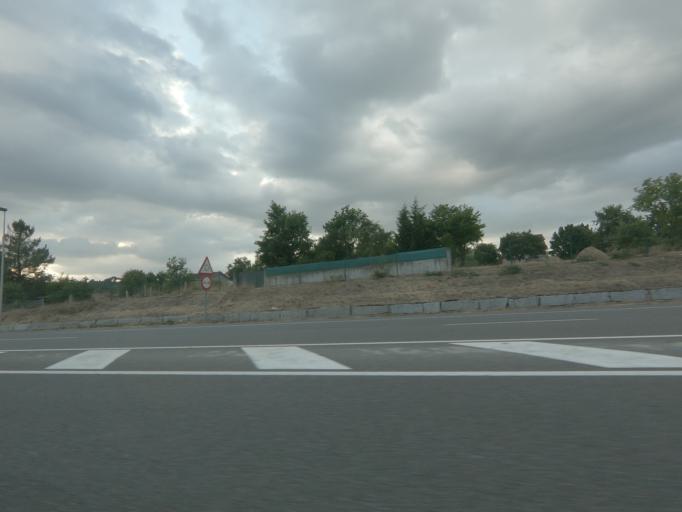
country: ES
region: Galicia
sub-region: Provincia de Ourense
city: Taboadela
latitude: 42.2855
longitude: -7.8346
